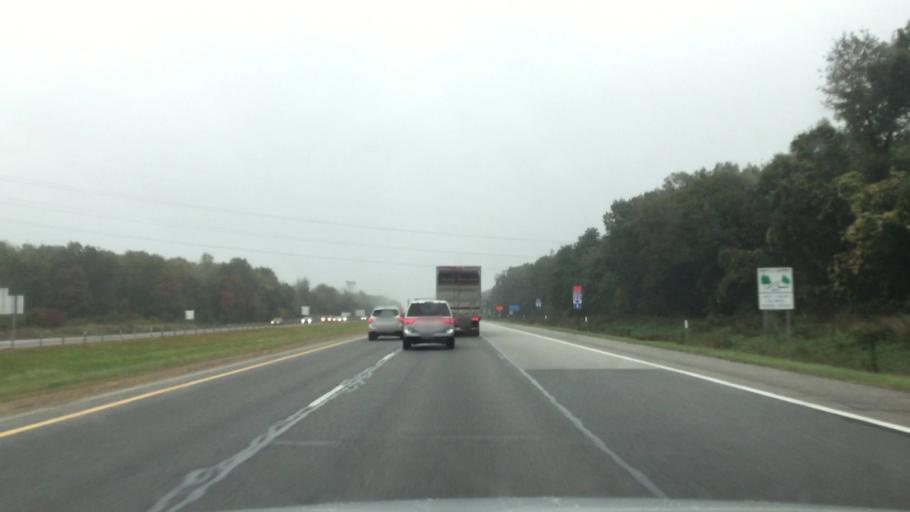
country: US
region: Michigan
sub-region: Kalamazoo County
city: Westwood
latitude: 42.2375
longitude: -85.6694
